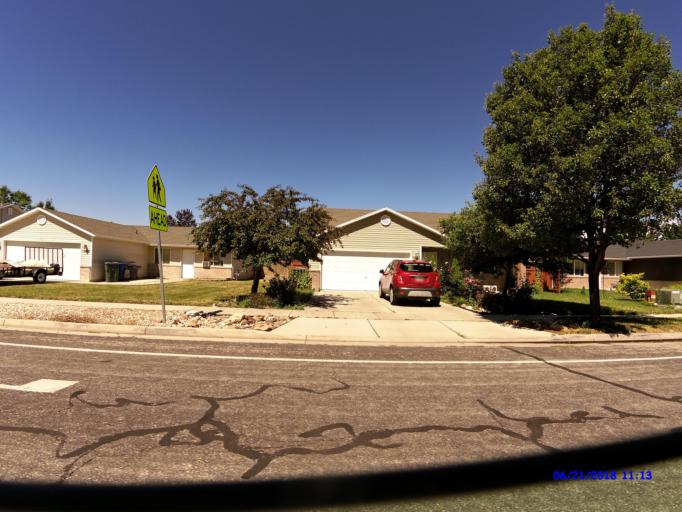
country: US
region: Utah
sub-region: Weber County
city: North Ogden
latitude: 41.2839
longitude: -111.9591
